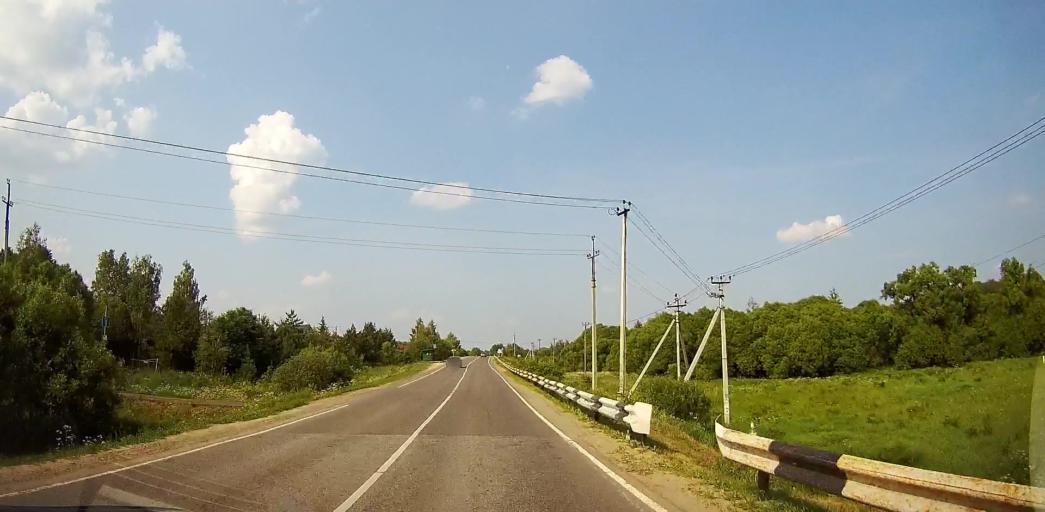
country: RU
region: Moskovskaya
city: Mikhnevo
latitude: 55.1822
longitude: 37.9743
